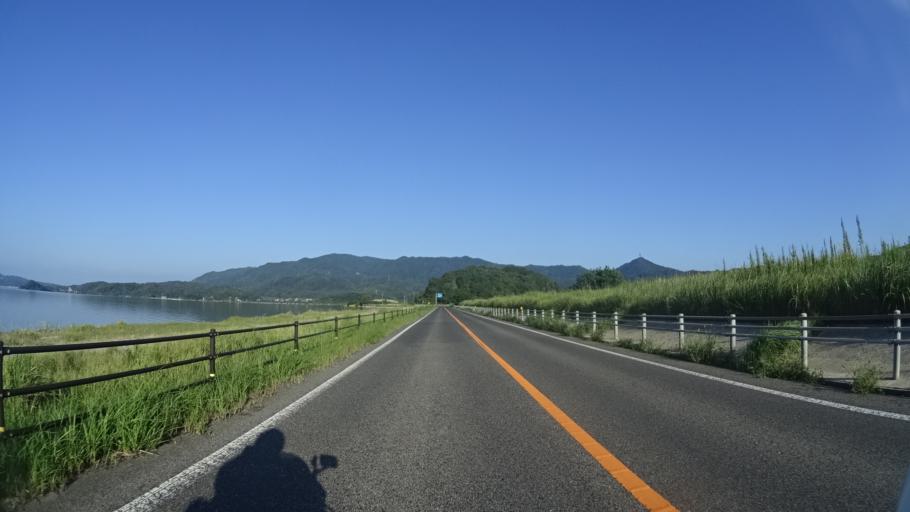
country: JP
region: Shimane
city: Sakaiminato
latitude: 35.5295
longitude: 133.1673
